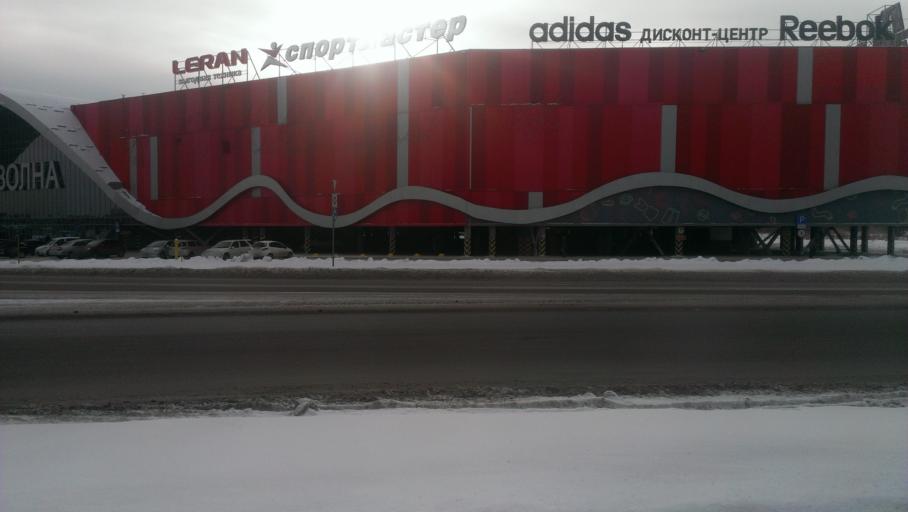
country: RU
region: Altai Krai
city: Novosilikatnyy
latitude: 53.3275
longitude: 83.6905
